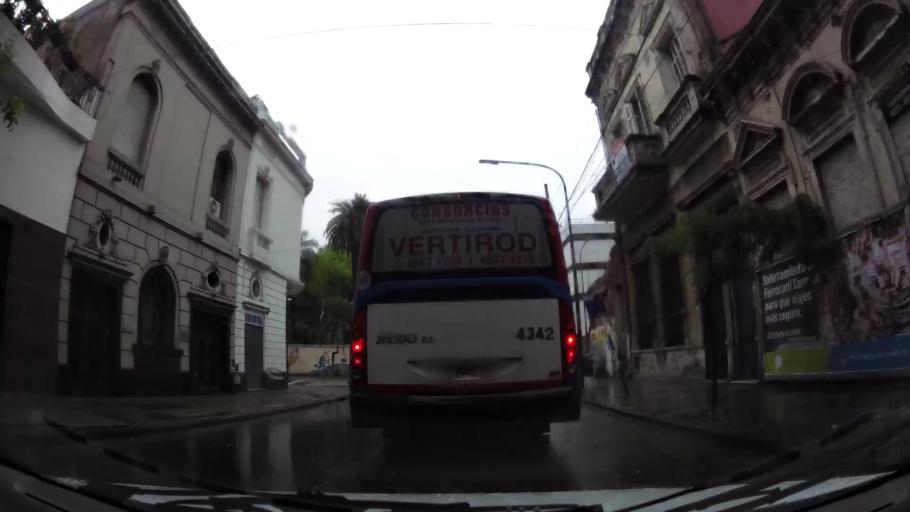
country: AR
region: Buenos Aires F.D.
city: Buenos Aires
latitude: -34.6248
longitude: -58.3897
